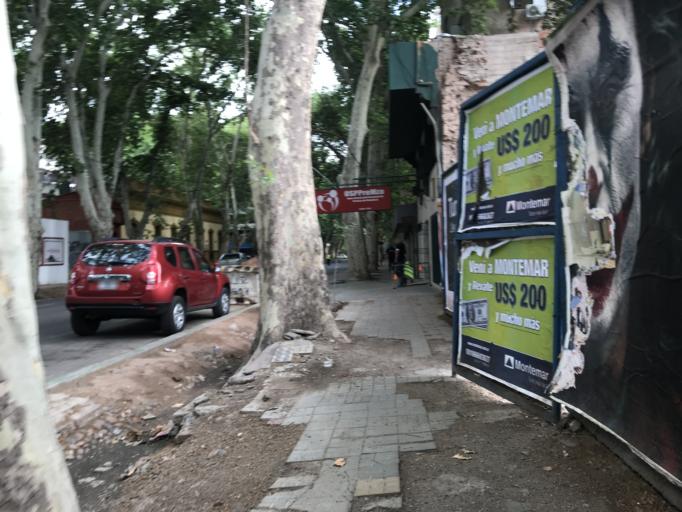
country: AR
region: Mendoza
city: Mendoza
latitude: -32.8838
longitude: -68.8442
